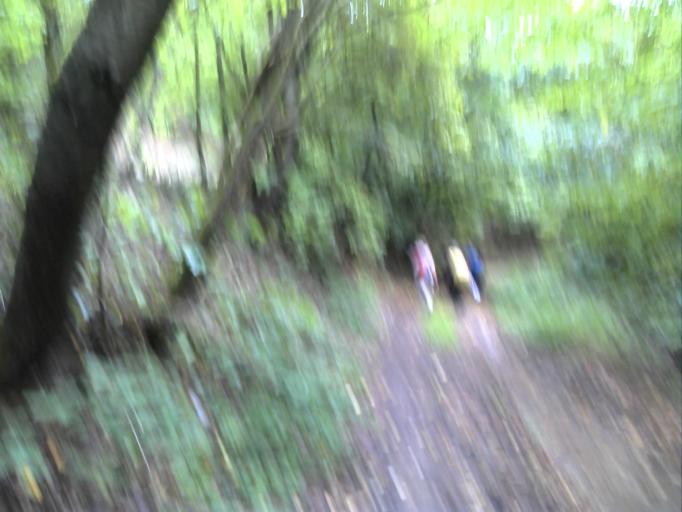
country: HU
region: Borsod-Abauj-Zemplen
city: Satoraljaujhely
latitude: 48.4091
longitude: 21.6165
